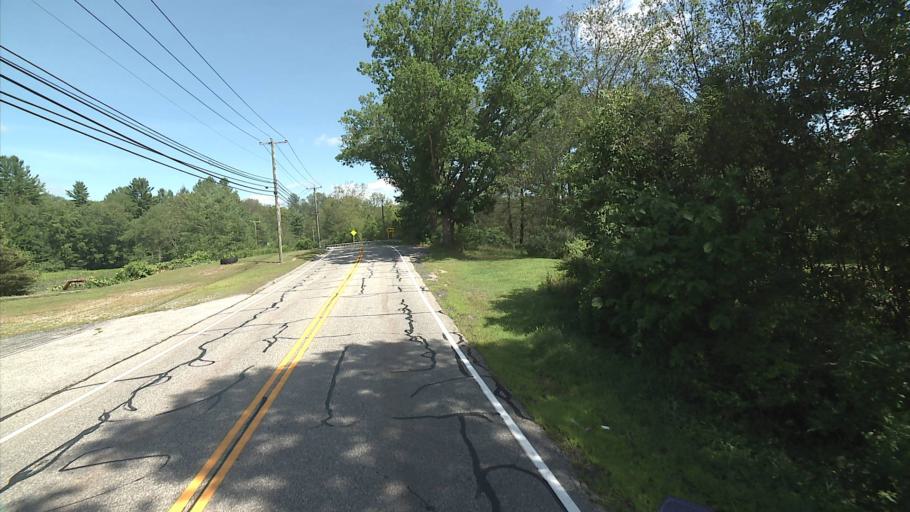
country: US
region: Connecticut
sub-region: Windham County
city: South Woodstock
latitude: 41.8807
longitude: -72.0848
